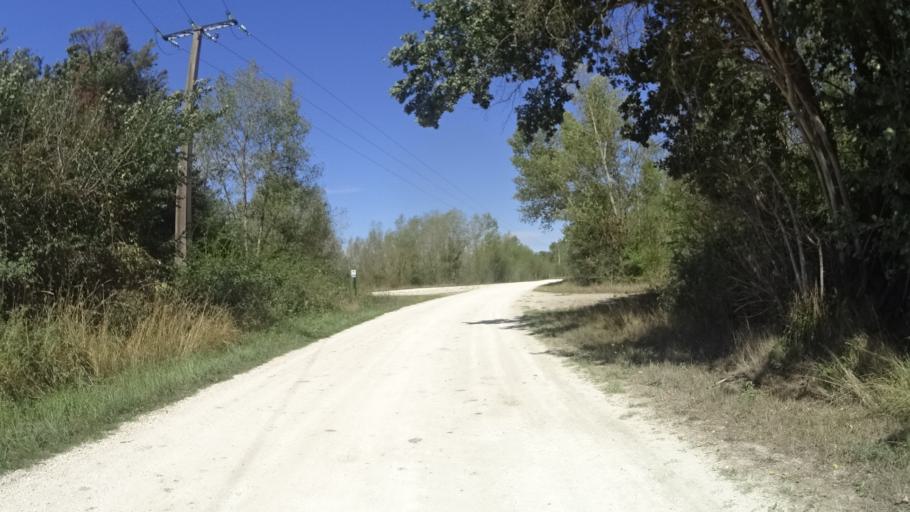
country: FR
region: Centre
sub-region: Departement du Loiret
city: Bonny-sur-Loire
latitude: 47.5438
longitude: 2.8362
